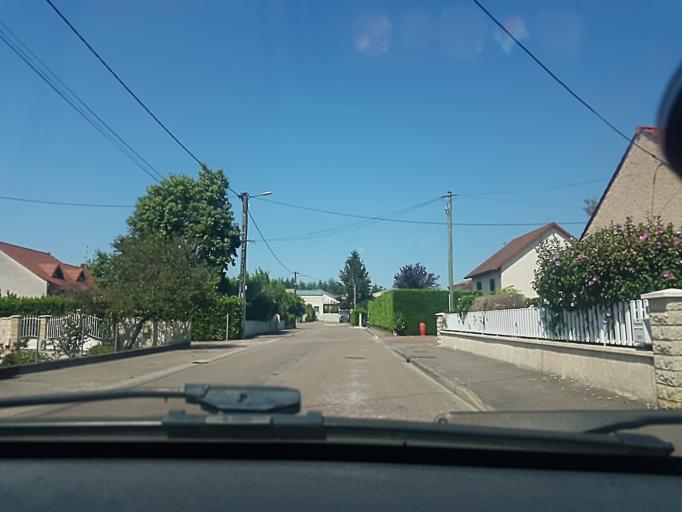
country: FR
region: Bourgogne
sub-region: Departement de Saone-et-Loire
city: Saint-Marcel
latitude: 46.7687
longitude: 4.8899
